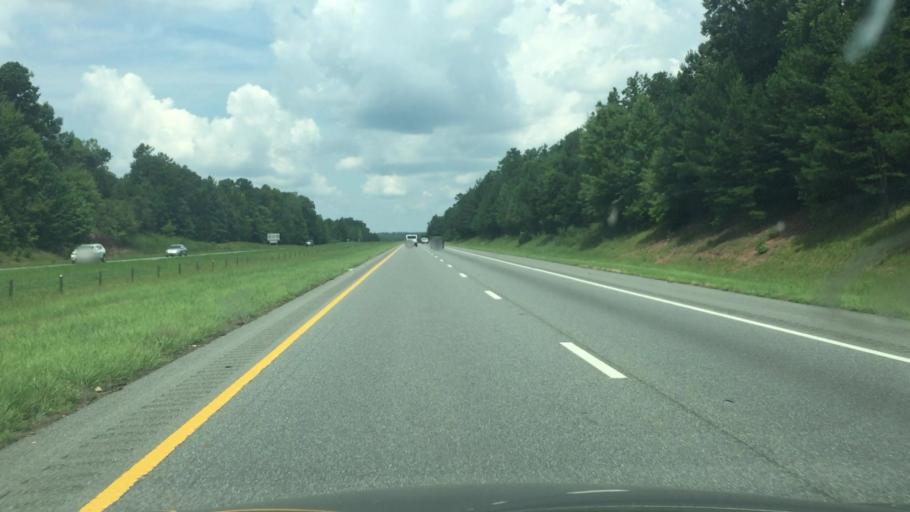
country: US
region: North Carolina
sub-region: Randolph County
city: Asheboro
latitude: 35.5481
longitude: -79.7967
